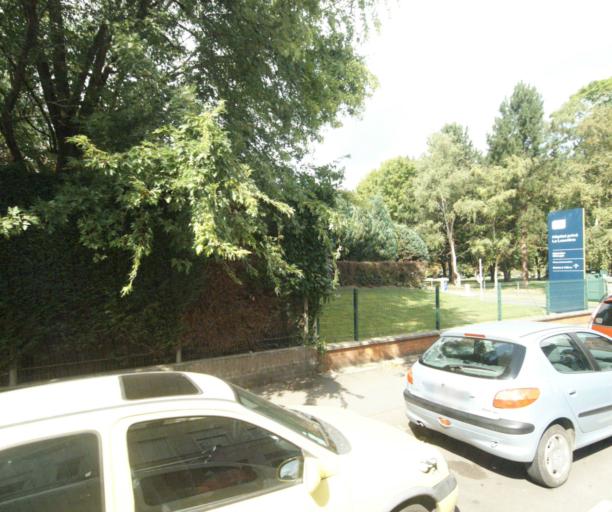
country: FR
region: Nord-Pas-de-Calais
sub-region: Departement du Nord
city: La Madeleine
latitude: 50.6460
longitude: 3.0858
